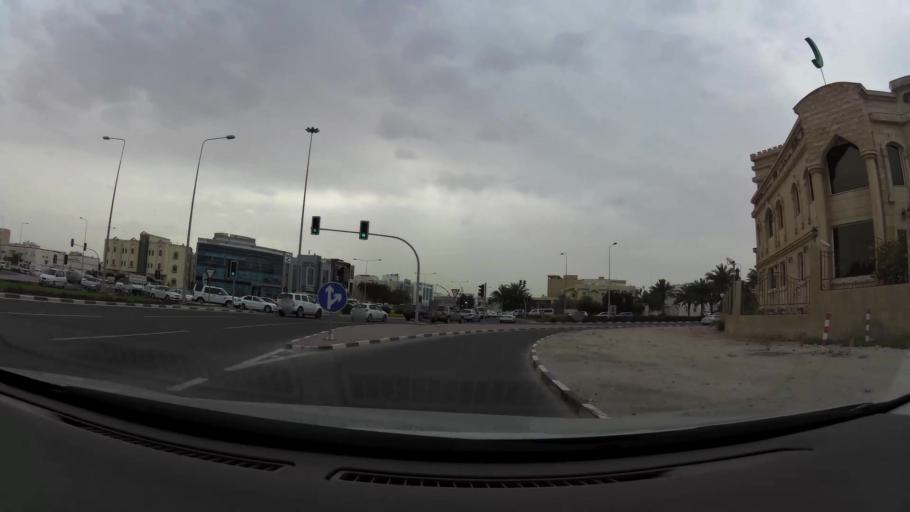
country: QA
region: Baladiyat ad Dawhah
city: Doha
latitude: 25.3072
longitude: 51.4886
